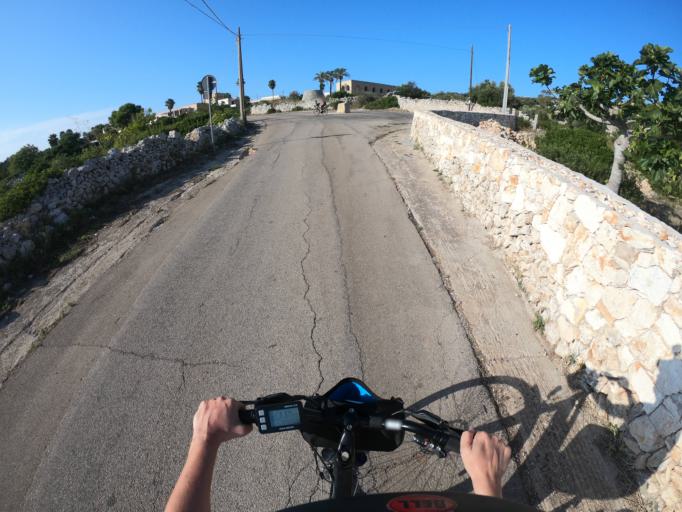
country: IT
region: Apulia
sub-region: Provincia di Lecce
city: Leuca
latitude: 39.8025
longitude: 18.3633
